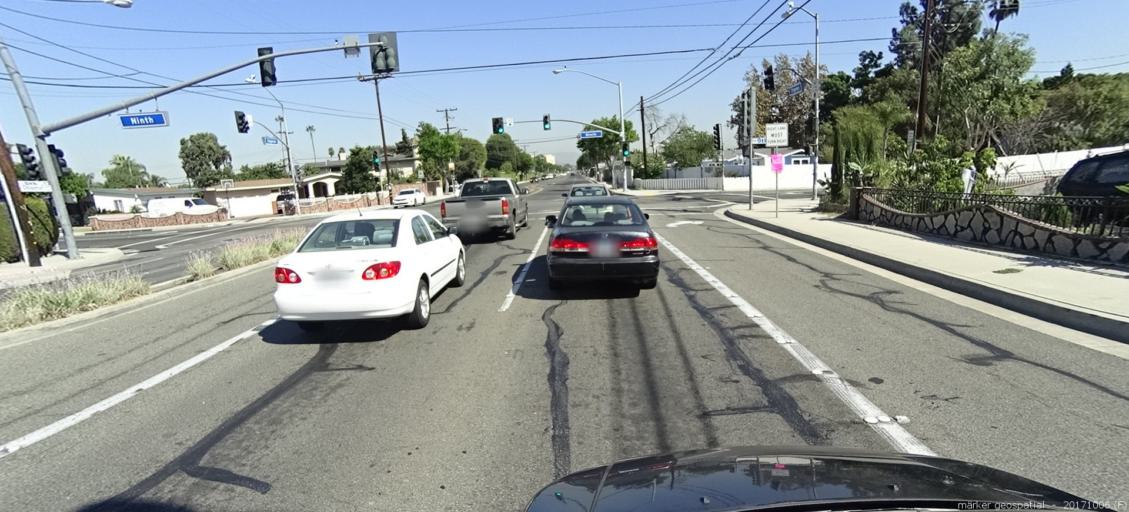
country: US
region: California
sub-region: Orange County
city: Garden Grove
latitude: 33.7887
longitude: -117.9330
